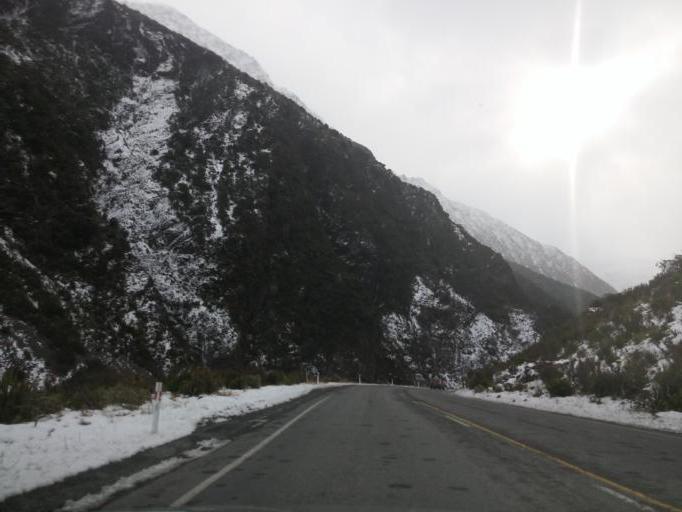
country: NZ
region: West Coast
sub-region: Grey District
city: Greymouth
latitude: -42.8894
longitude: 171.5561
